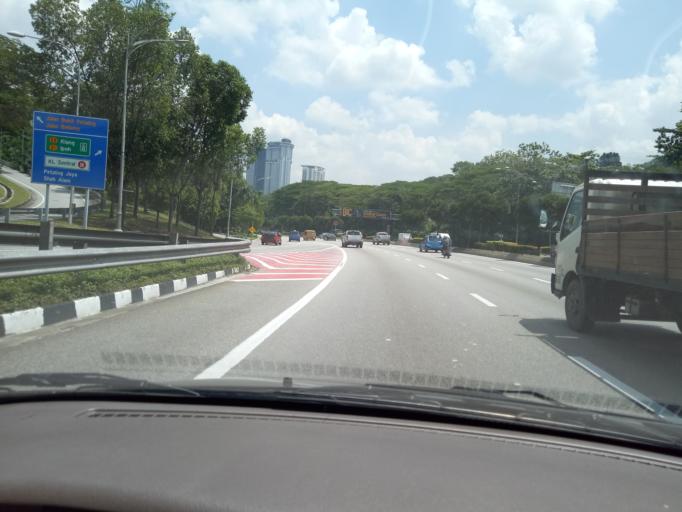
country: MY
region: Kuala Lumpur
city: Kuala Lumpur
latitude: 3.1311
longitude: 101.7011
